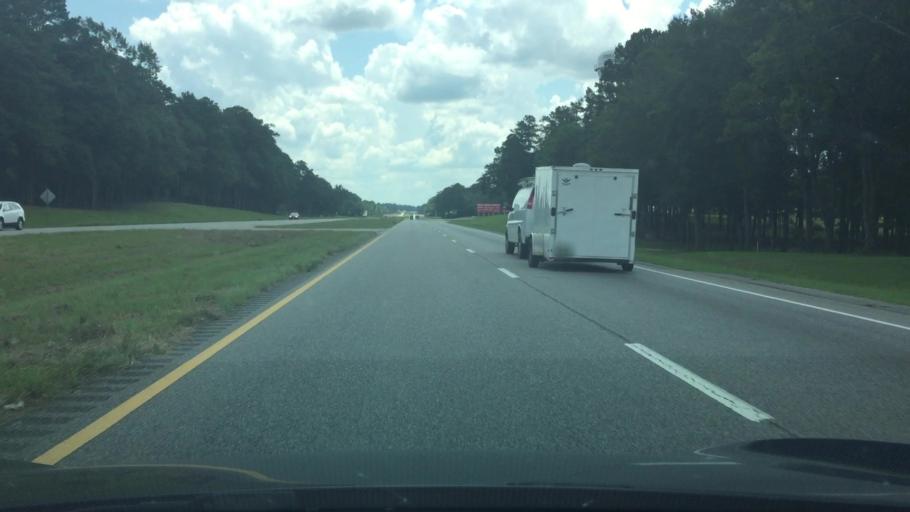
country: US
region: Alabama
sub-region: Montgomery County
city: Taylor
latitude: 32.0669
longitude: -86.0576
